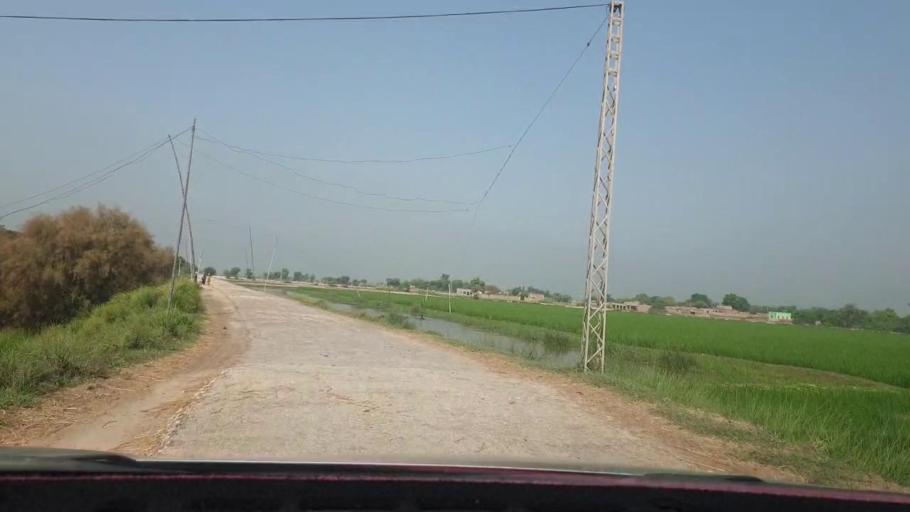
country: PK
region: Sindh
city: Nasirabad
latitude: 27.4326
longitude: 67.8924
